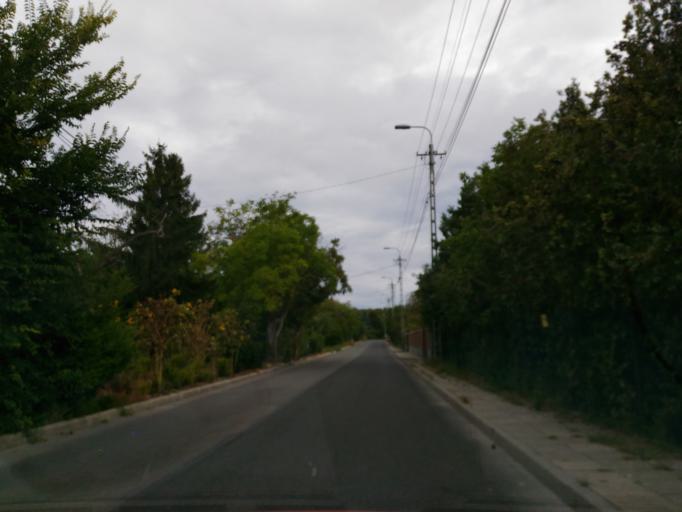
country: HU
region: Pest
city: Diosd
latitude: 47.4039
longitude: 18.9760
